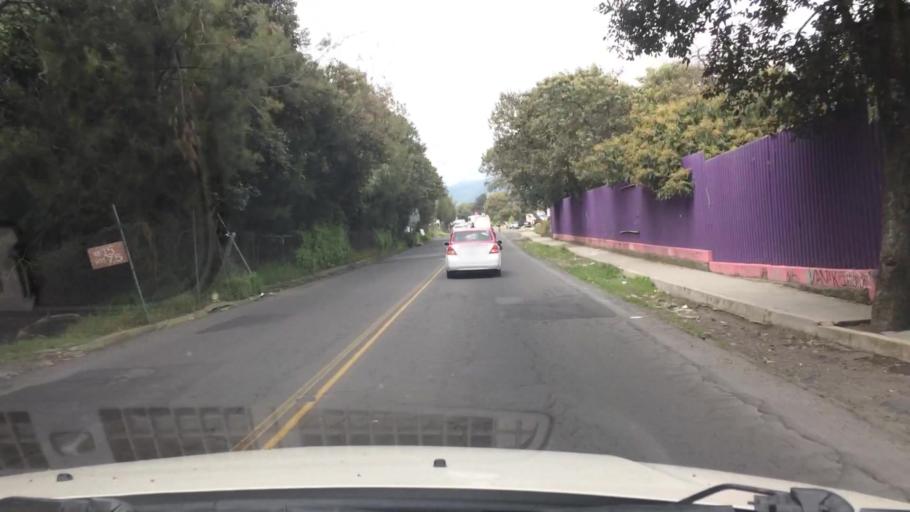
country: MX
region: Mexico City
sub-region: Tlalpan
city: Lomas de Tepemecatl
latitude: 19.2680
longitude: -99.2204
